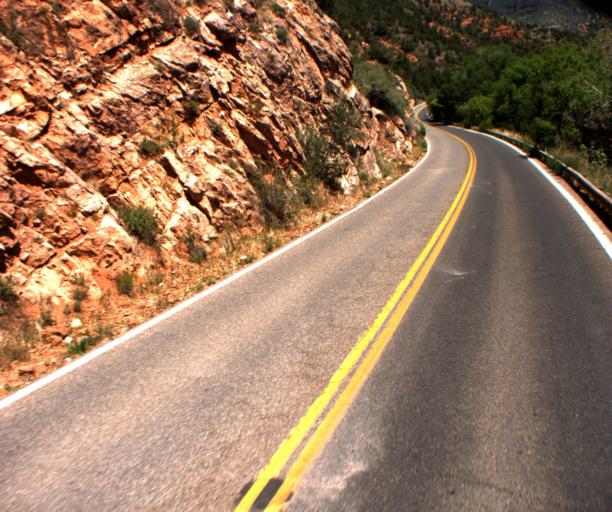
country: US
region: Arizona
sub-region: Coconino County
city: Sedona
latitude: 34.8968
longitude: -111.7321
